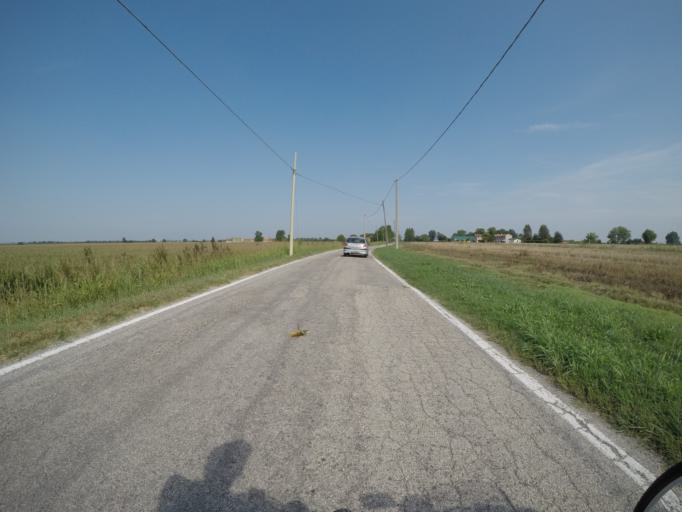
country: IT
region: Veneto
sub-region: Provincia di Rovigo
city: Villanova del Ghebbo Canton
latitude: 45.0575
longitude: 11.6280
